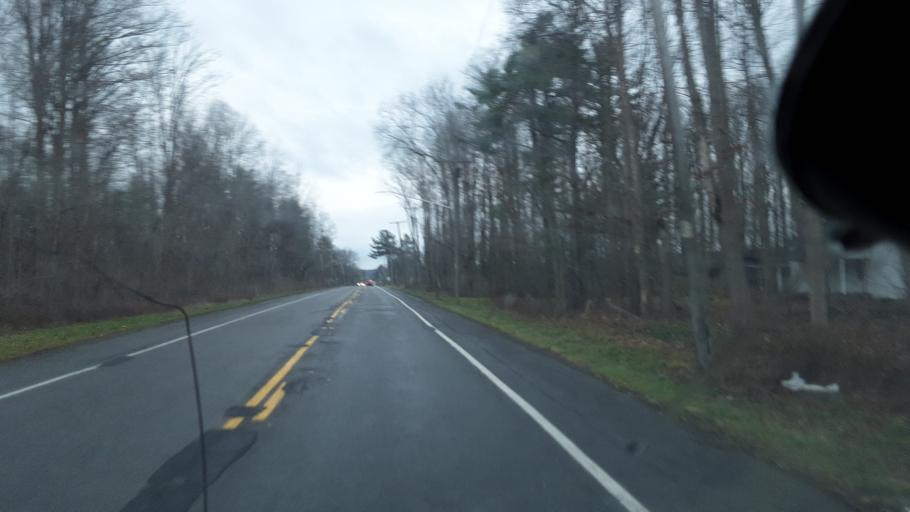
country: US
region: New York
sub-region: Erie County
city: Holland
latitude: 42.6675
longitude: -78.5581
